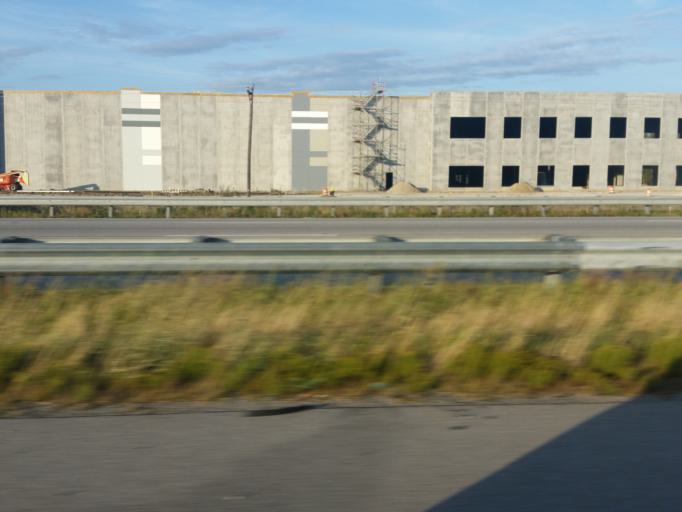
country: US
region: Indiana
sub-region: Boone County
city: Whitestown
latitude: 39.9691
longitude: -86.3806
